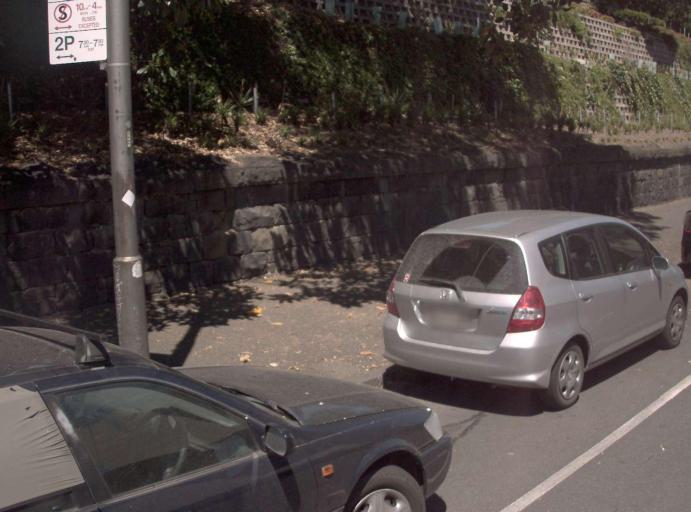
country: AU
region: Victoria
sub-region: Melbourne
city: West Melbourne
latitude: -37.8104
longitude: 144.9530
